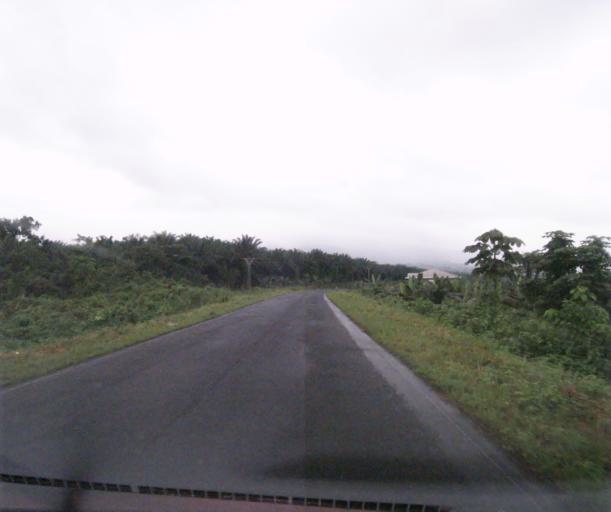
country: CM
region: South-West Province
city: Idenao
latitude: 4.2017
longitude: 9.0003
